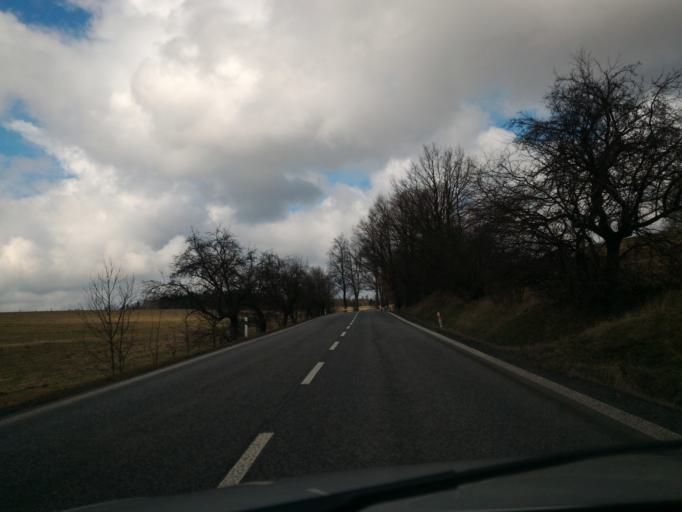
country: PL
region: Silesian Voivodeship
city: Zawidow
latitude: 50.9824
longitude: 15.0759
